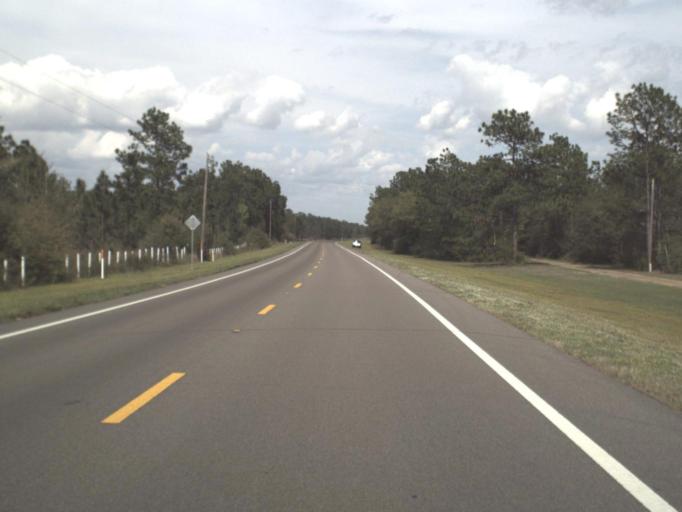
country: US
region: Florida
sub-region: Santa Rosa County
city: East Milton
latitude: 30.6821
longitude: -86.8361
